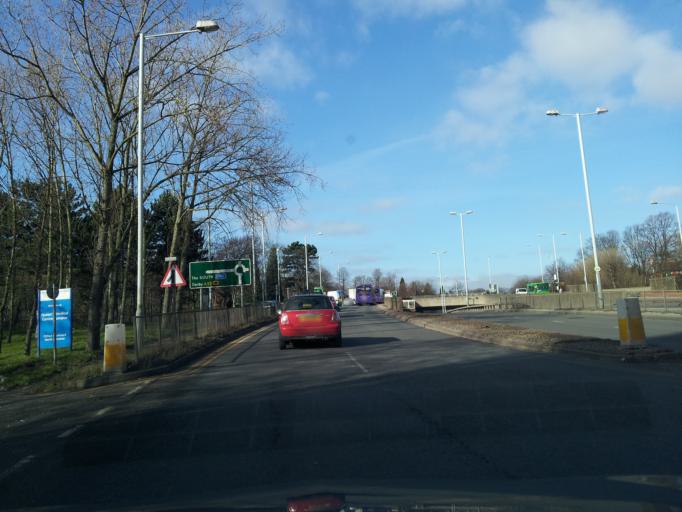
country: GB
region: England
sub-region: Nottingham
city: Nottingham
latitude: 52.9429
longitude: -1.1886
